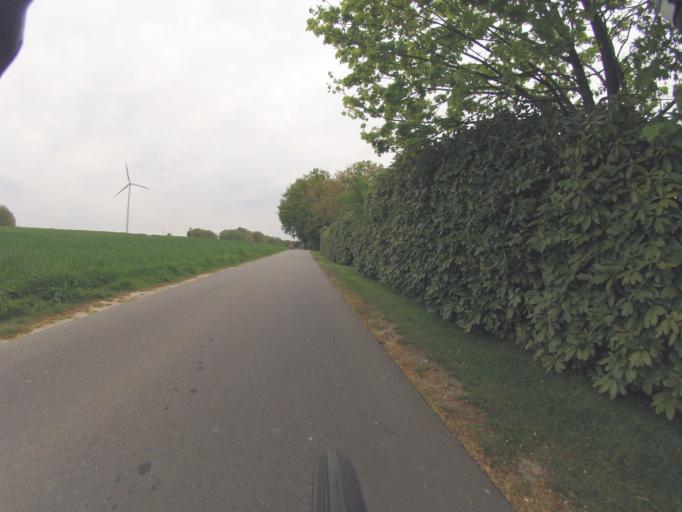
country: DE
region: North Rhine-Westphalia
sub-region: Regierungsbezirk Munster
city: Westerkappeln
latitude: 52.3055
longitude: 7.8426
